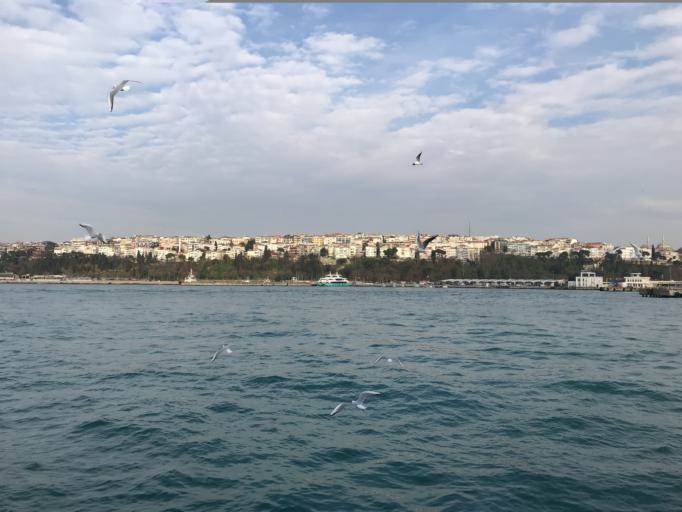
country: TR
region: Istanbul
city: UEskuedar
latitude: 41.0112
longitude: 29.0047
